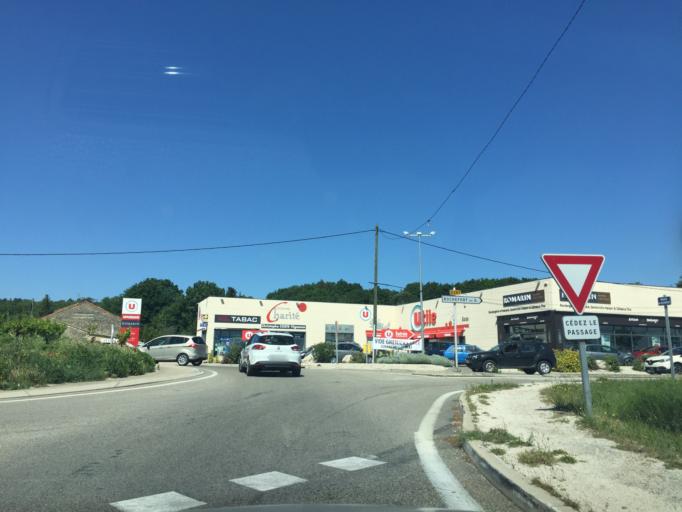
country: FR
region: Languedoc-Roussillon
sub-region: Departement du Gard
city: Saze
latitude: 43.9470
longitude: 4.6844
